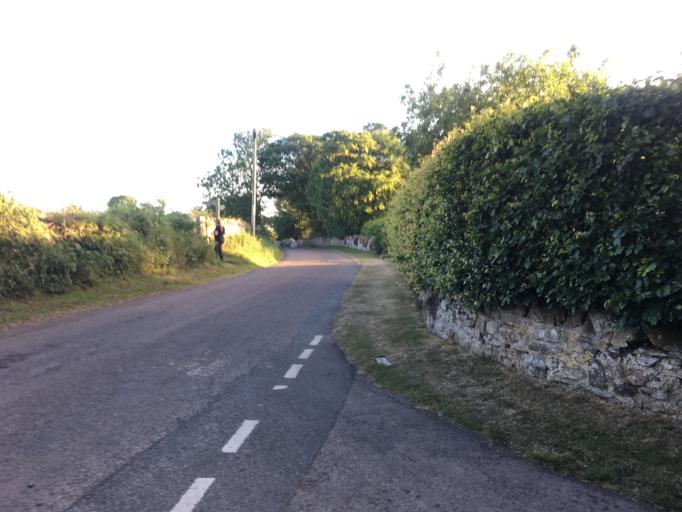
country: GB
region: England
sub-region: Northumberland
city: North Sunderland
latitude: 55.5867
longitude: -1.6777
